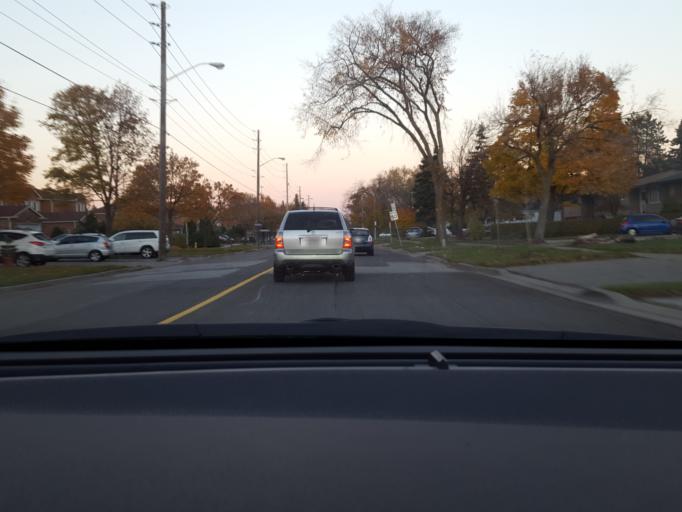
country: CA
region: Ontario
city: Scarborough
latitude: 43.7936
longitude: -79.1588
